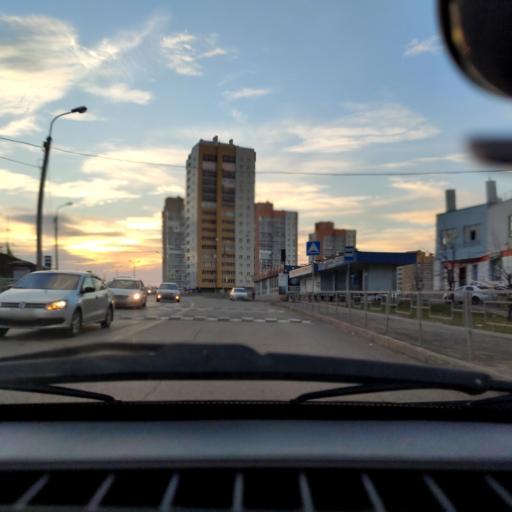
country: RU
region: Bashkortostan
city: Ufa
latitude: 54.6895
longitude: 55.9933
